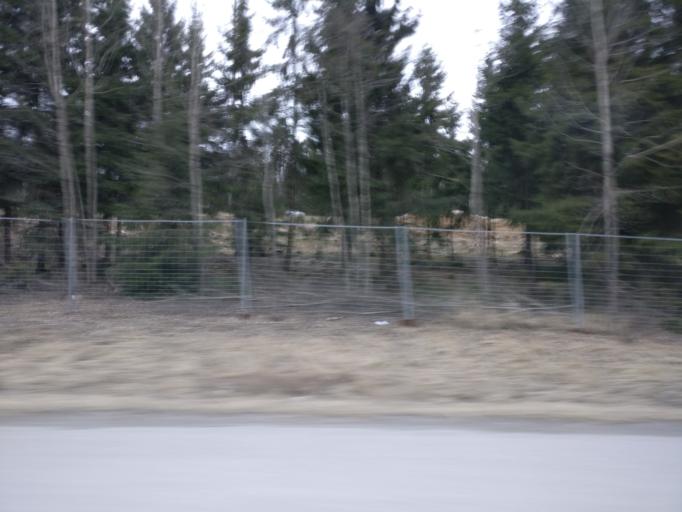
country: FI
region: Uusimaa
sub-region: Helsinki
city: Nurmijaervi
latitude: 60.3645
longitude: 24.8087
